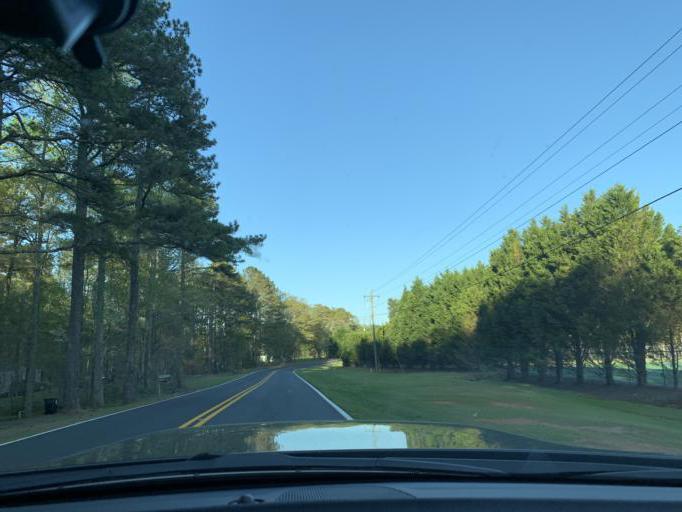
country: US
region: Georgia
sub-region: Forsyth County
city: Cumming
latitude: 34.2596
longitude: -84.2159
